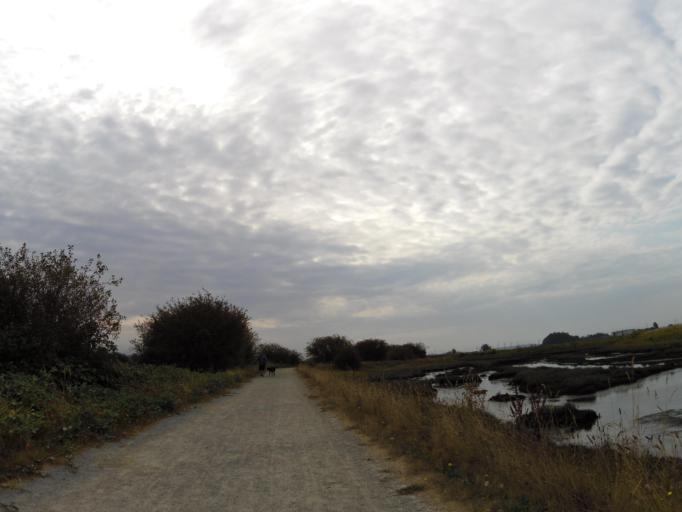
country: US
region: Washington
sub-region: Skagit County
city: Mount Vernon
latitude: 48.4581
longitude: -122.4693
